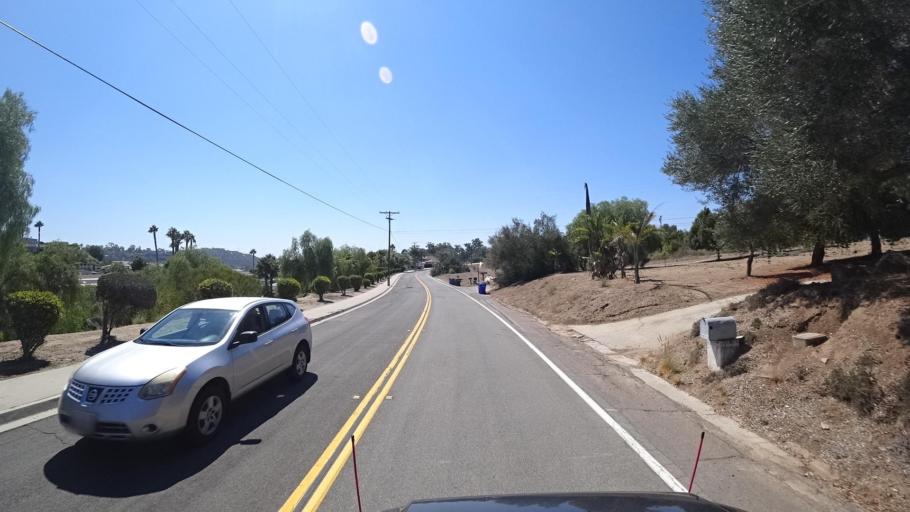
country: US
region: California
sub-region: San Diego County
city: Lake San Marcos
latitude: 33.1396
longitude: -117.2156
